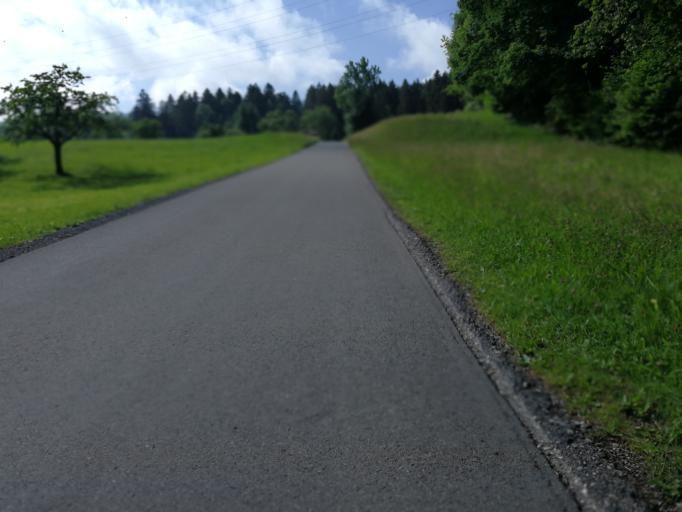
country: CH
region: Schwyz
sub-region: Bezirk Hoefe
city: Freienbach
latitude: 47.1849
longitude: 8.7743
